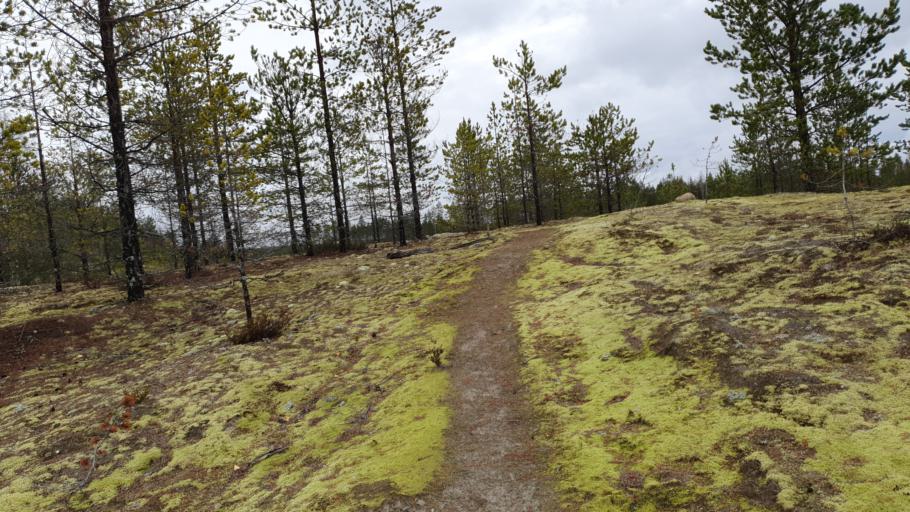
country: FI
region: Kainuu
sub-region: Kehys-Kainuu
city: Kuhmo
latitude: 64.1516
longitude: 29.3959
